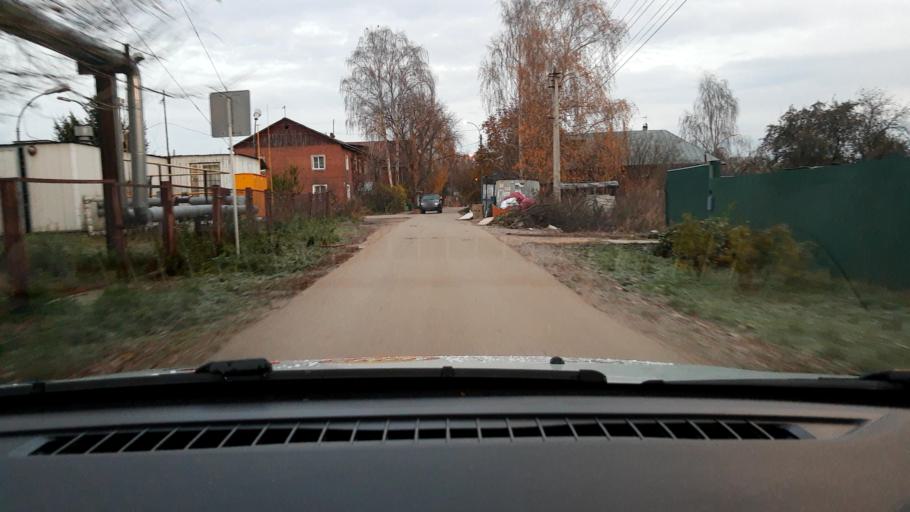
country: RU
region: Nizjnij Novgorod
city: Afonino
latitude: 56.2689
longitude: 44.0937
